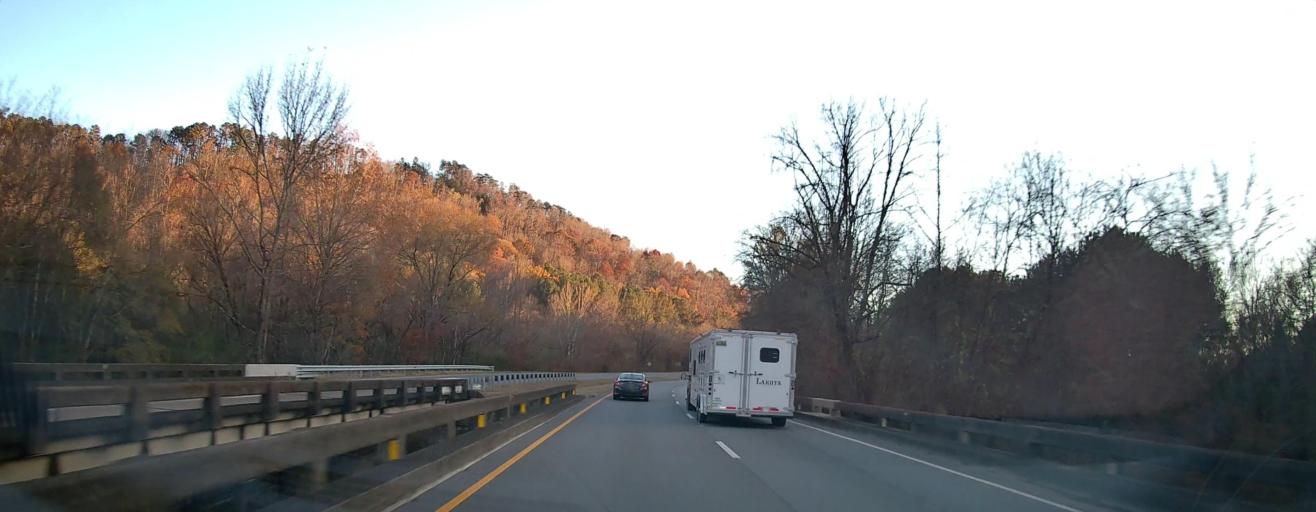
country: US
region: Alabama
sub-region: Etowah County
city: Attalla
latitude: 34.0335
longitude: -86.1107
